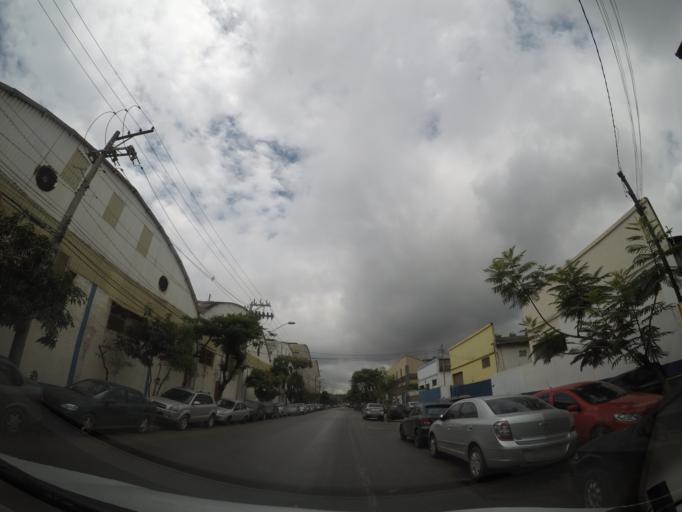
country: BR
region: Sao Paulo
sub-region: Guarulhos
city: Guarulhos
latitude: -23.4677
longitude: -46.4861
